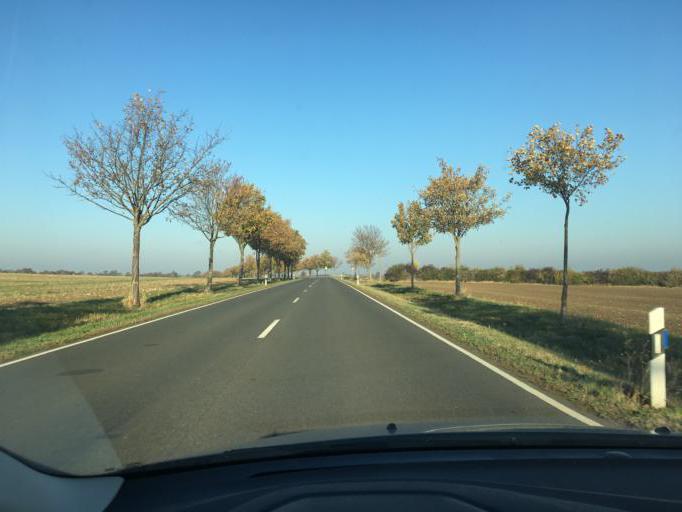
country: DE
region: Saxony-Anhalt
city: Wanzleben
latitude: 52.0324
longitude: 11.4764
